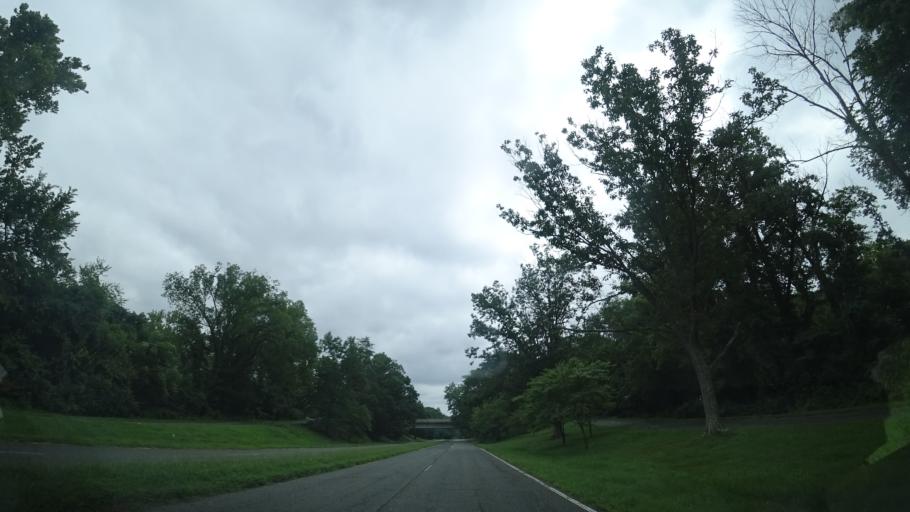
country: US
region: Maryland
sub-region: Montgomery County
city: Cabin John
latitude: 38.9719
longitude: -77.1545
